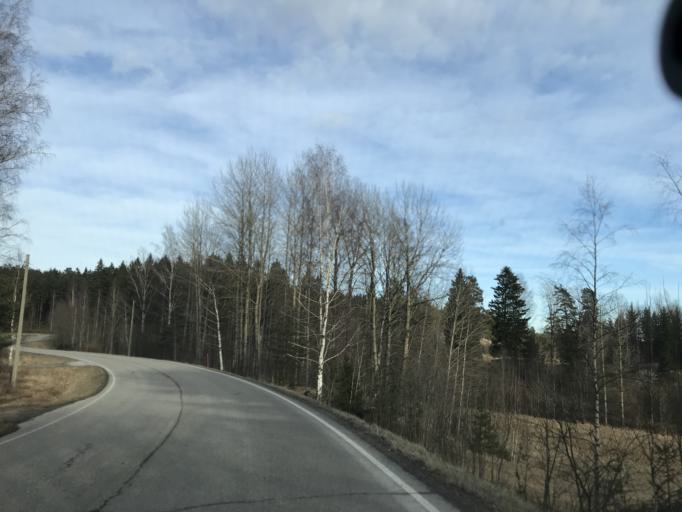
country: FI
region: Uusimaa
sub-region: Raaseporin
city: Pohja
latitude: 60.0892
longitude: 23.4280
